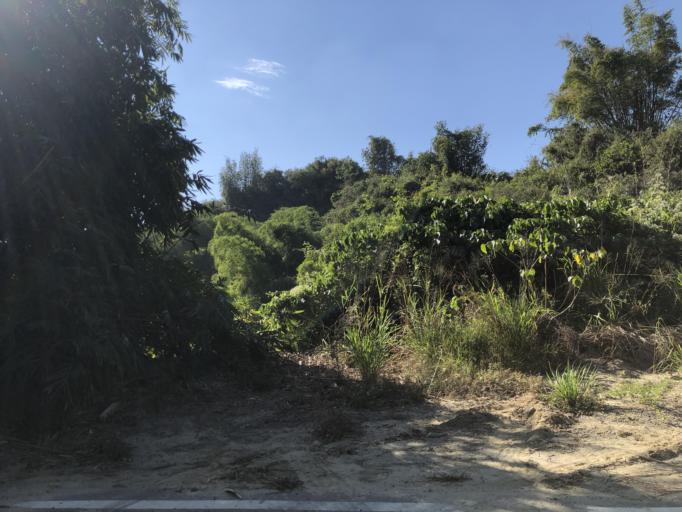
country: TW
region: Taiwan
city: Yujing
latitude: 23.0435
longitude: 120.3970
